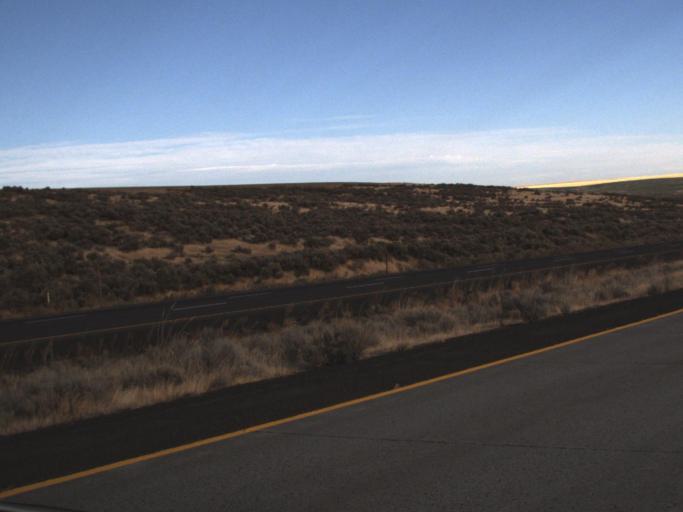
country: US
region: Washington
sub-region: Adams County
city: Ritzville
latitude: 46.9542
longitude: -118.5755
